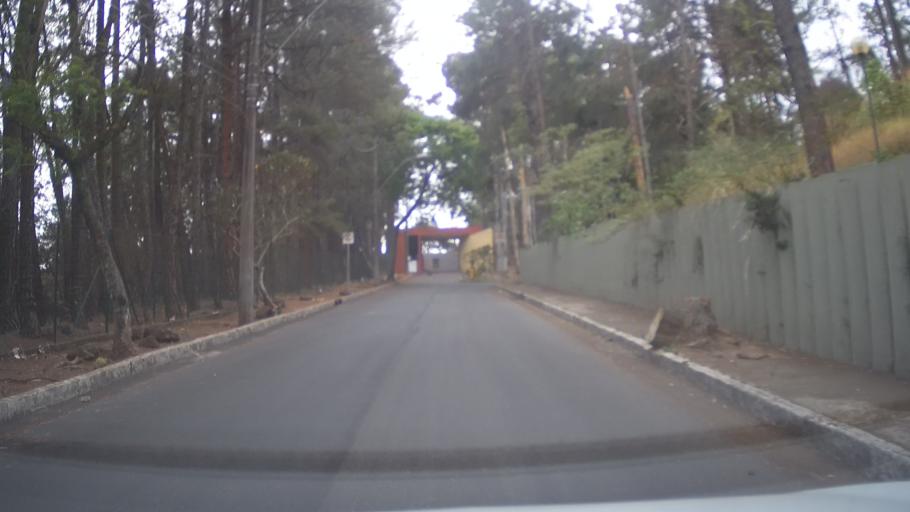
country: BR
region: Minas Gerais
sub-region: Belo Horizonte
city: Belo Horizonte
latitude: -19.9531
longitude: -43.9133
